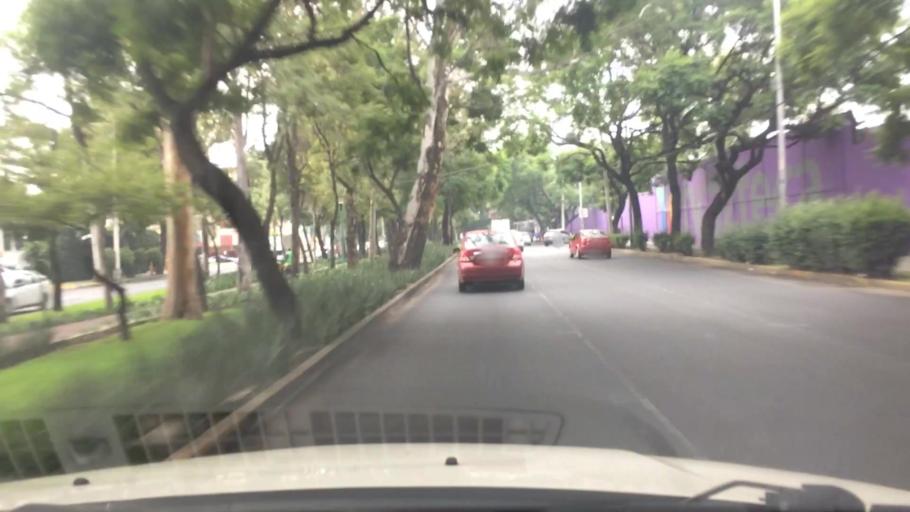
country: MX
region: Mexico City
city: Coyoacan
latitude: 19.3243
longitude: -99.1354
